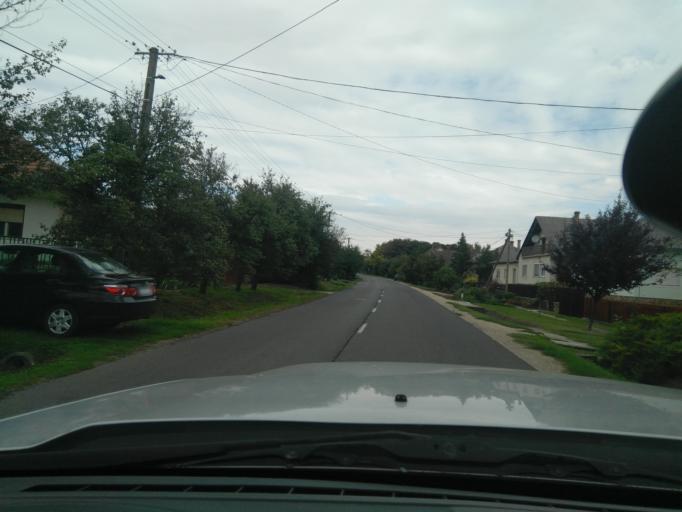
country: HU
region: Fejer
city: Val
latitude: 47.3619
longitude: 18.7364
